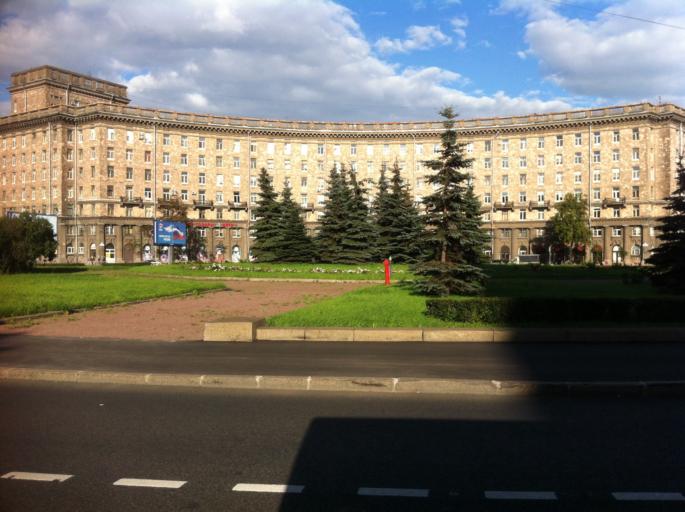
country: RU
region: St.-Petersburg
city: Avtovo
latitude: 59.8764
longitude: 30.2565
